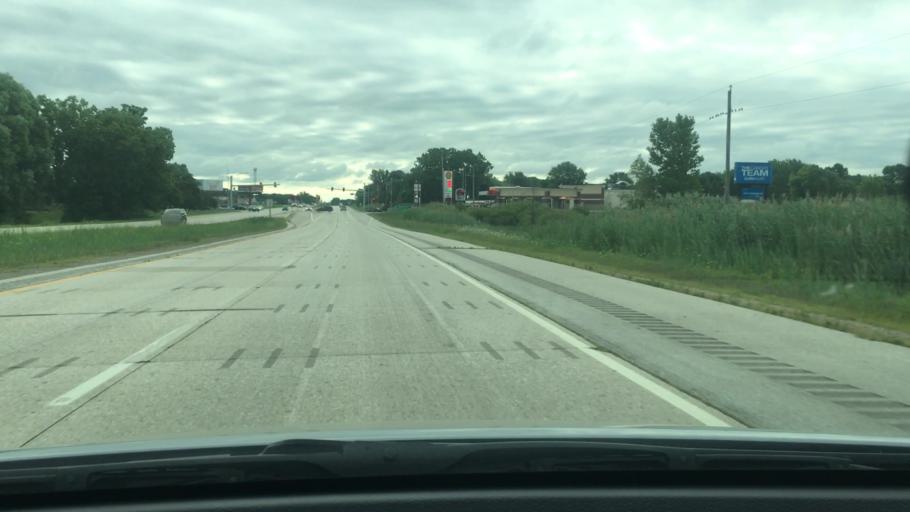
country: US
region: Wisconsin
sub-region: Brown County
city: Ashwaubenon
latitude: 44.4932
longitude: -88.1009
